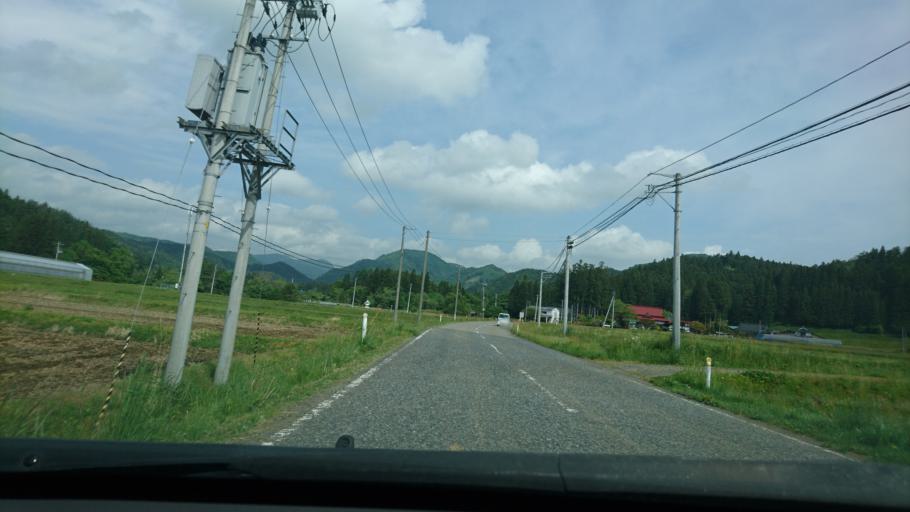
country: JP
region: Iwate
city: Ichinoseki
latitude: 38.8912
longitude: 140.9477
